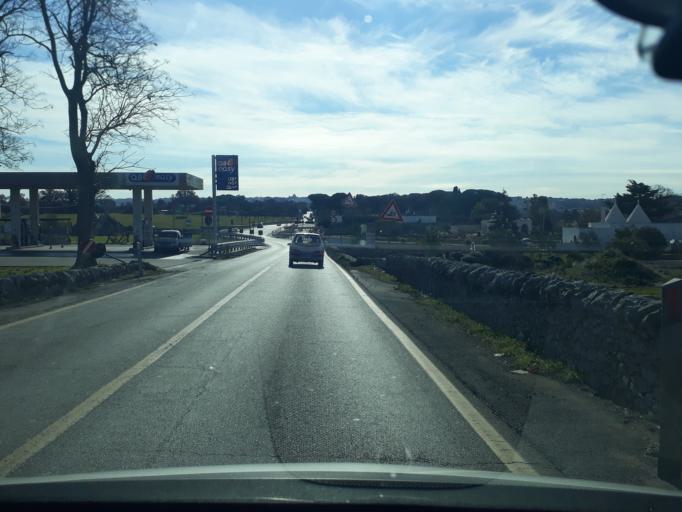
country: IT
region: Apulia
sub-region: Provincia di Bari
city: Locorotondo
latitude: 40.7376
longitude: 17.3325
